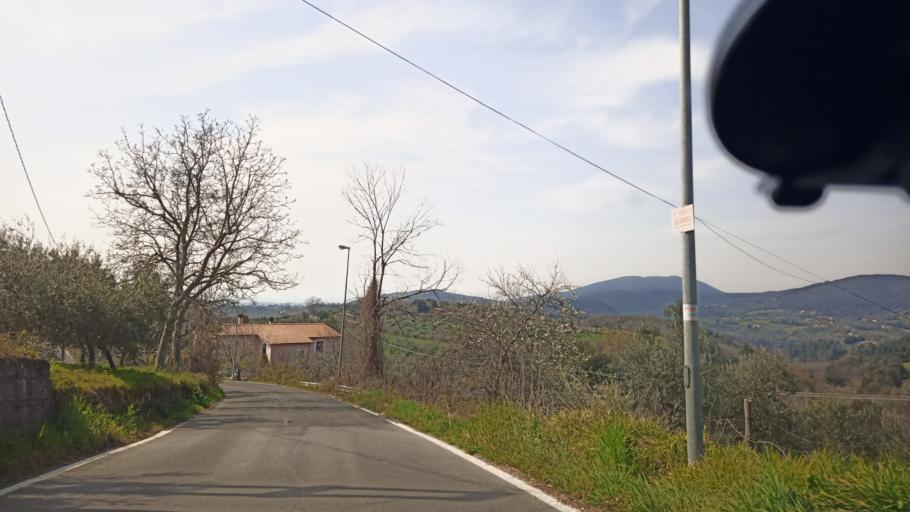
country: IT
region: Latium
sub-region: Provincia di Rieti
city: Montasola
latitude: 42.3652
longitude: 12.6757
